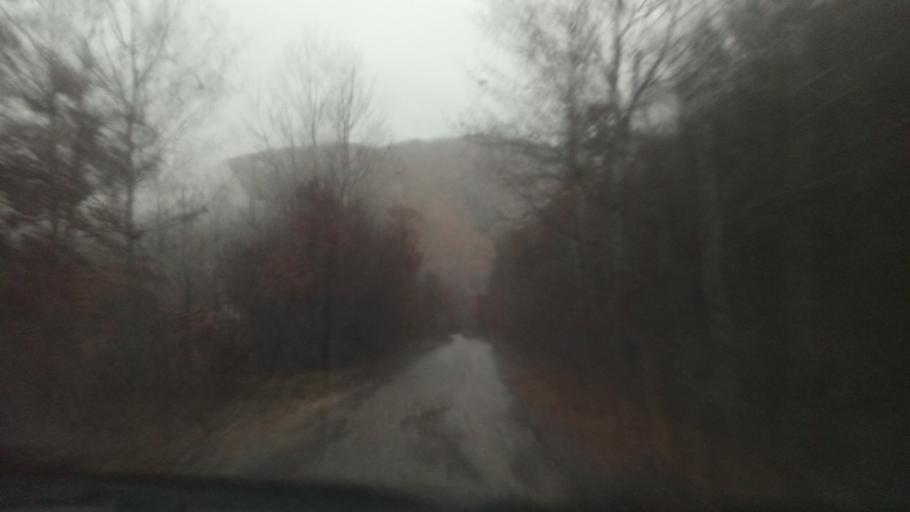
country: MK
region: Vinica
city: Blatec
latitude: 41.8398
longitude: 22.6119
